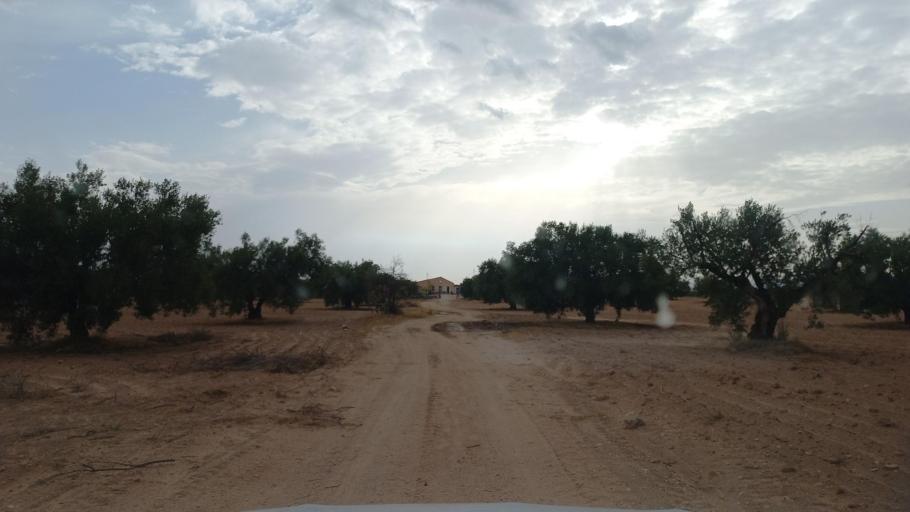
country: TN
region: Al Qasrayn
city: Sbiba
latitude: 35.2961
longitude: 9.0783
